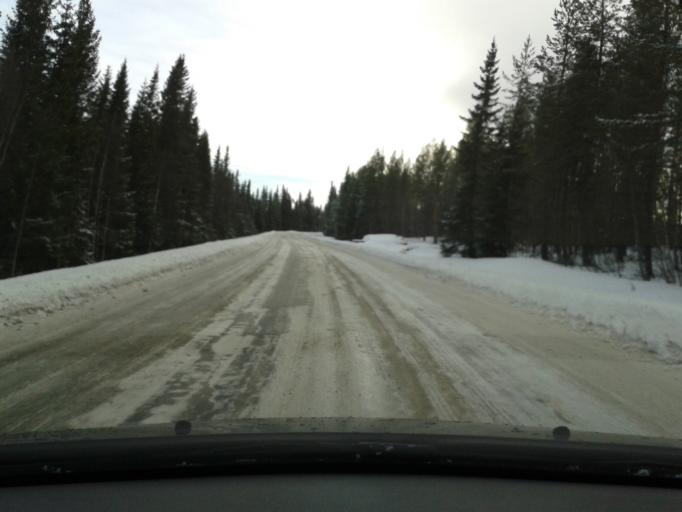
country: SE
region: Vaesterbotten
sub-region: Vilhelmina Kommun
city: Sjoberg
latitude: 64.7572
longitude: 16.1588
